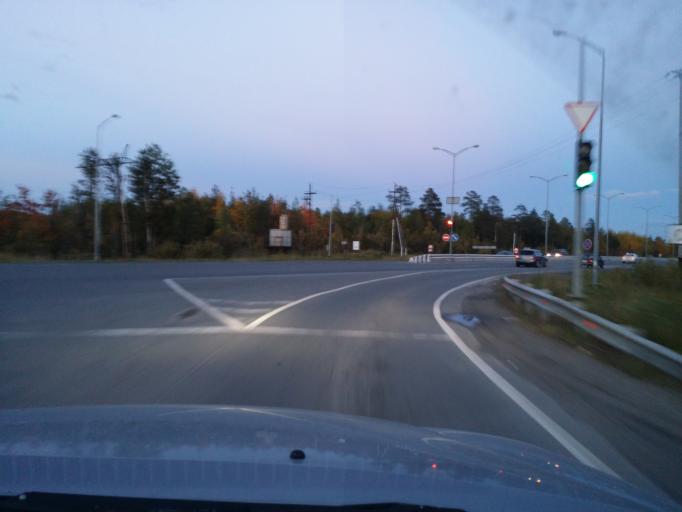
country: RU
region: Khanty-Mansiyskiy Avtonomnyy Okrug
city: Nizhnevartovsk
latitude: 60.9916
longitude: 76.4347
